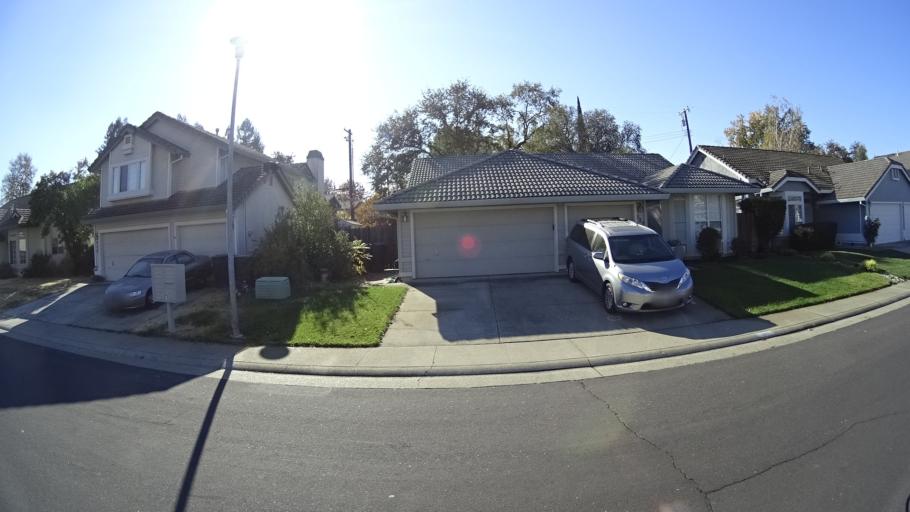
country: US
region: California
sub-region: Sacramento County
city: Citrus Heights
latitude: 38.7223
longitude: -121.3027
